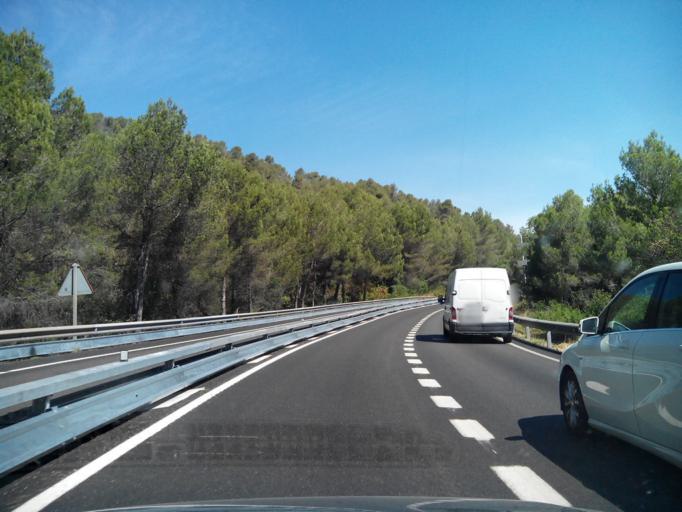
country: ES
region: Catalonia
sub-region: Provincia de Barcelona
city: Viladecavalls
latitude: 41.5760
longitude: 1.9611
